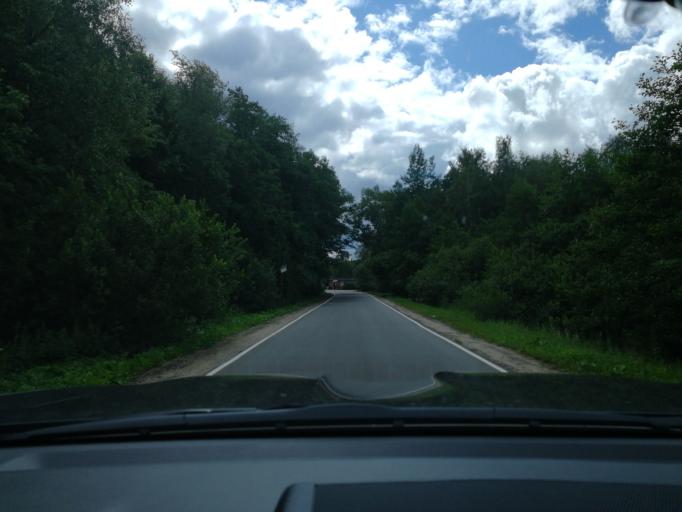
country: RU
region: Moskovskaya
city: Proletarskiy
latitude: 55.0100
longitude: 37.4757
